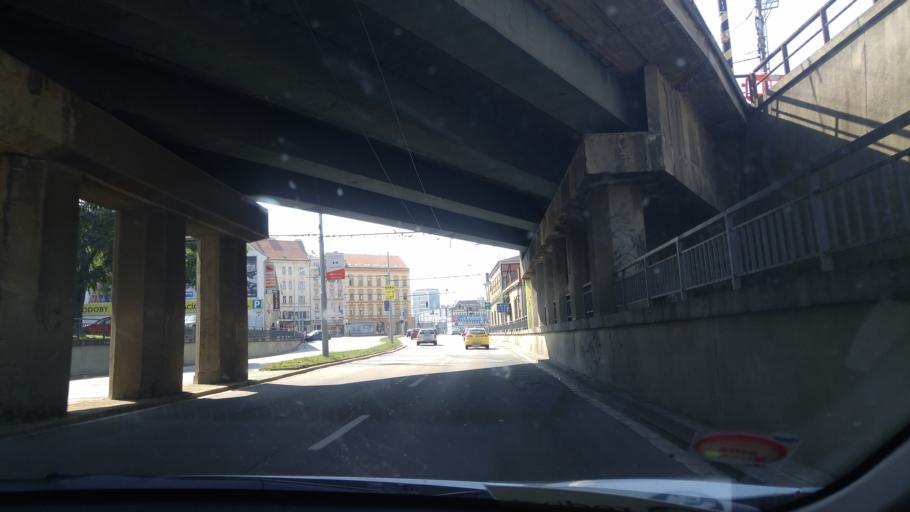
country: CZ
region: South Moravian
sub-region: Mesto Brno
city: Brno
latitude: 49.1932
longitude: 16.6156
